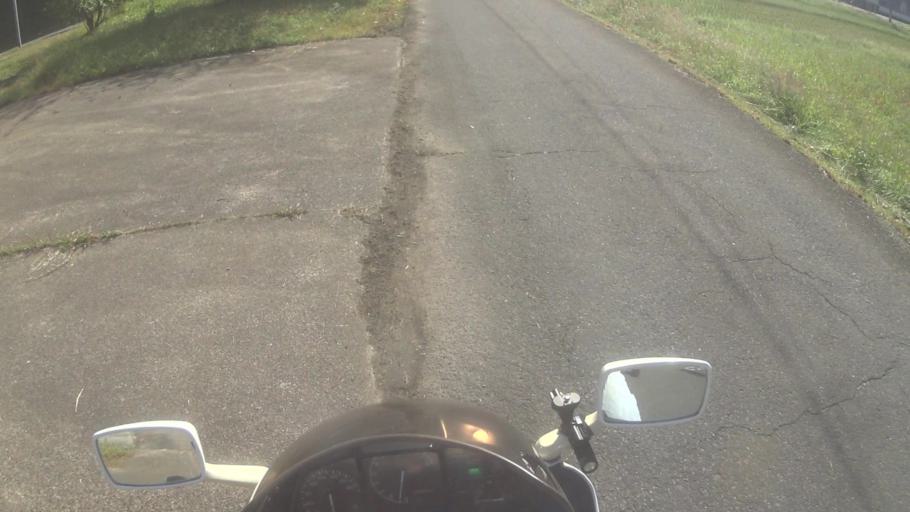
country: JP
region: Kyoto
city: Miyazu
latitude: 35.6706
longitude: 135.0725
